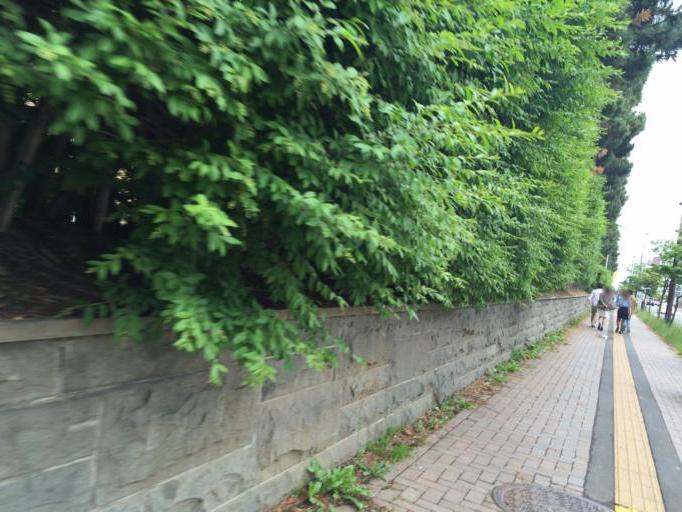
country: JP
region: Hokkaido
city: Sapporo
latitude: 43.0770
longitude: 141.3462
